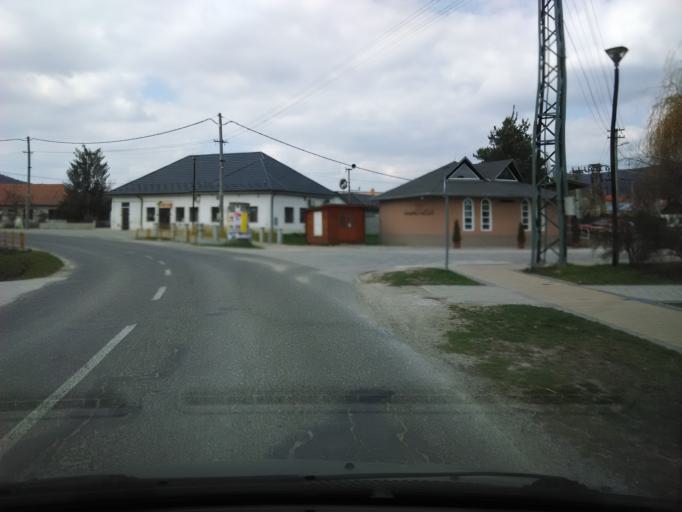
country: SK
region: Nitriansky
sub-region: Okres Nitra
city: Nitra
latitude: 48.3793
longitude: 18.2243
